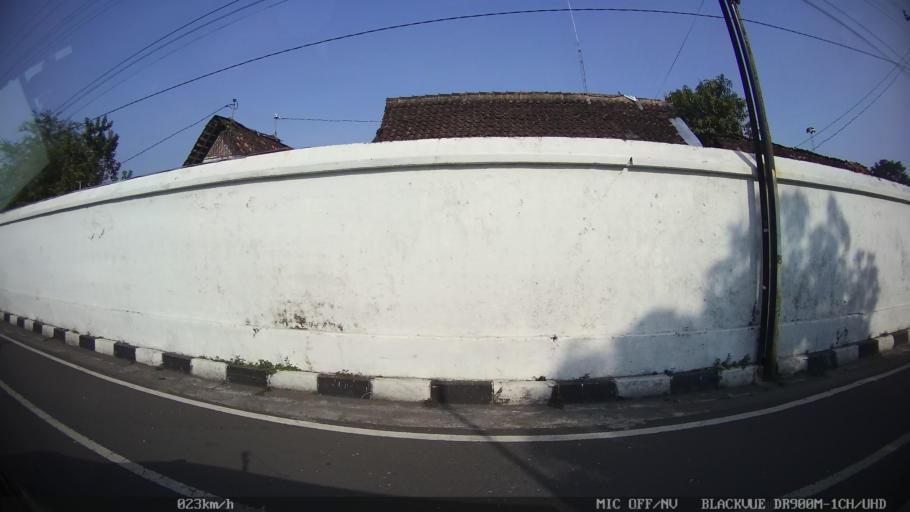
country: ID
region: Daerah Istimewa Yogyakarta
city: Yogyakarta
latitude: -7.8105
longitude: 110.3607
